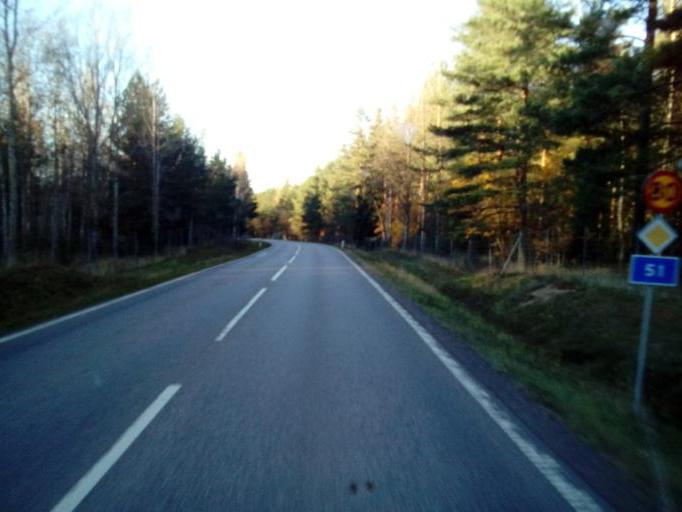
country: SE
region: OErebro
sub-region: Hallsbergs Kommun
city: Palsboda
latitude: 59.0051
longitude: 15.4033
